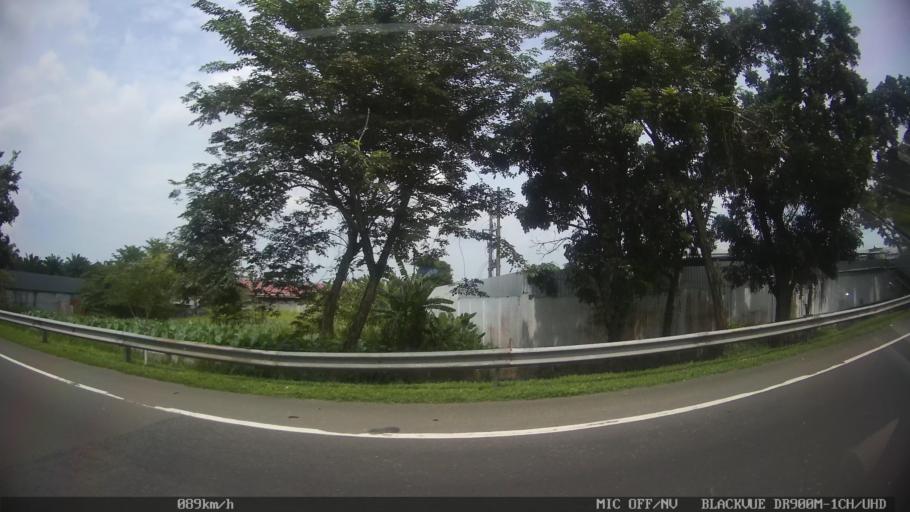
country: ID
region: North Sumatra
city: Labuhan Deli
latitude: 3.6866
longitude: 98.6817
